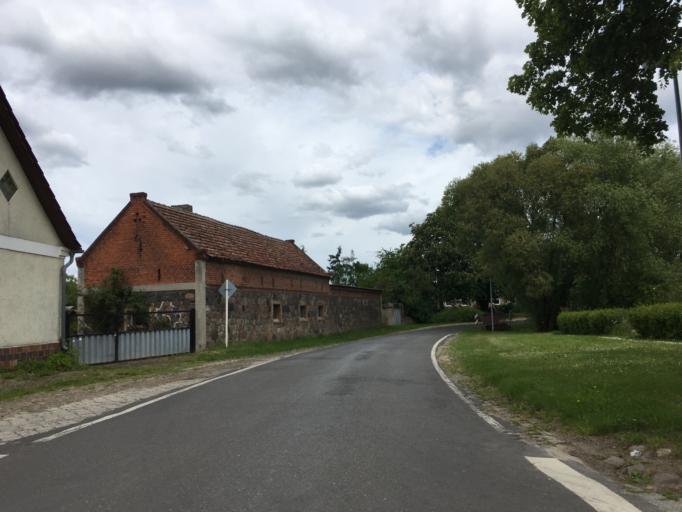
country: DE
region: Brandenburg
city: Hohenfinow
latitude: 52.7582
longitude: 13.8781
